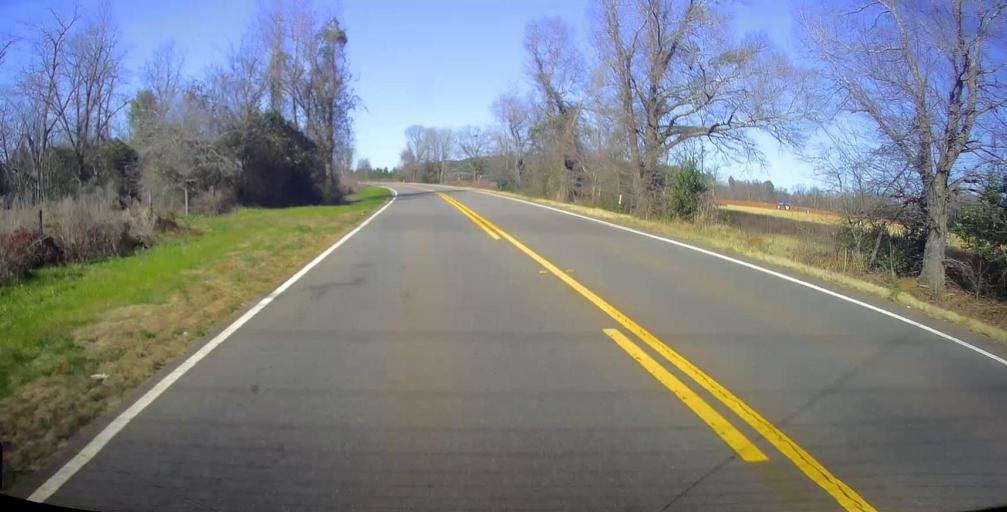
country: US
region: Georgia
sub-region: Macon County
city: Montezuma
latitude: 32.3872
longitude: -84.0157
